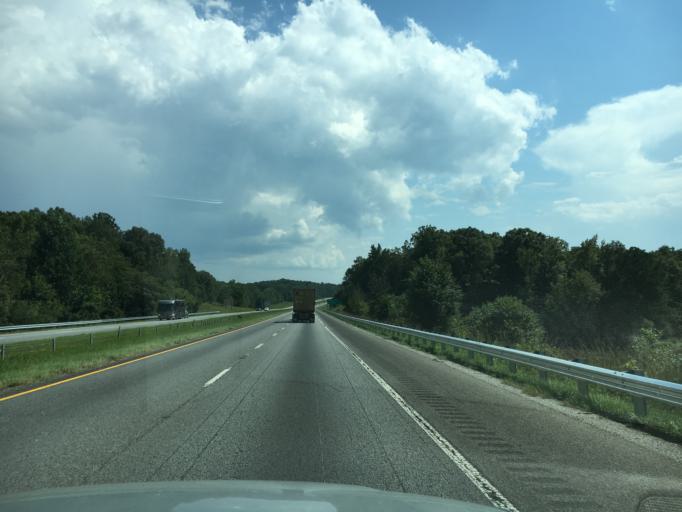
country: US
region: South Carolina
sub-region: Spartanburg County
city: Roebuck
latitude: 34.8277
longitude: -81.9665
